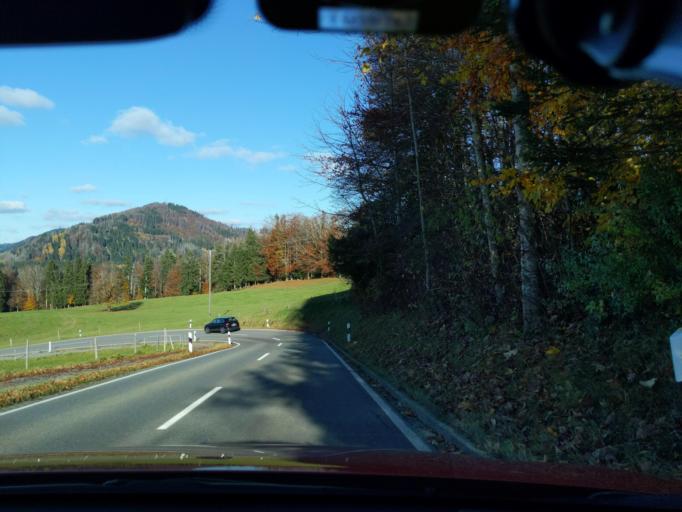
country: DE
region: Bavaria
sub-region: Swabia
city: Oberstaufen
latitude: 47.5340
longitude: 10.0243
